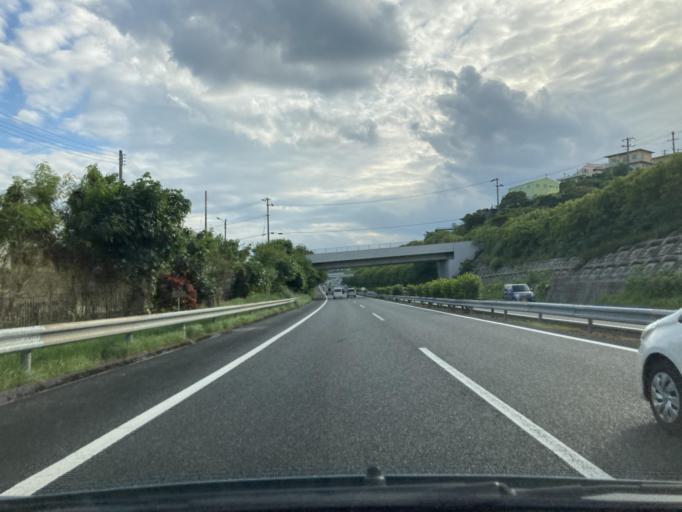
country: JP
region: Okinawa
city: Ginowan
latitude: 26.2691
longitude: 127.7756
